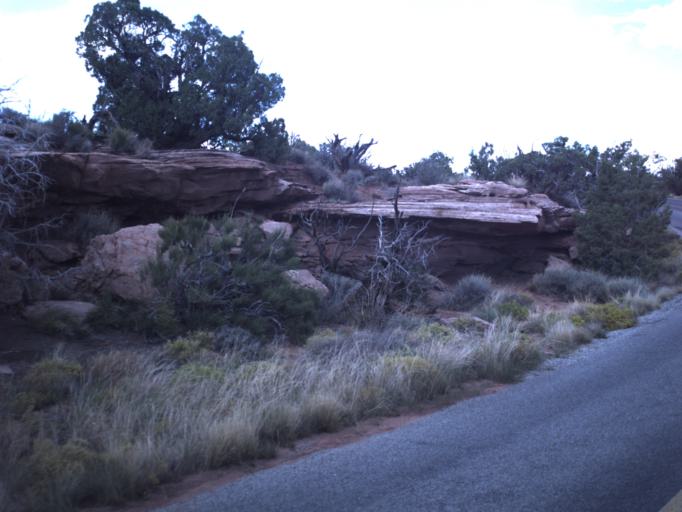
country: US
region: Utah
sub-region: Grand County
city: Moab
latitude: 38.4770
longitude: -109.7411
